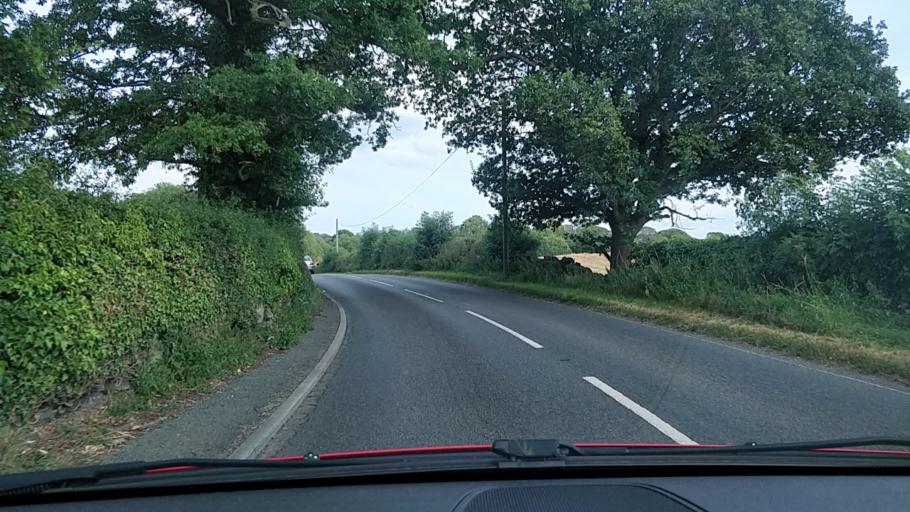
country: GB
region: Wales
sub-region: County of Flintshire
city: Penyffordd
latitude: 53.1414
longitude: -3.0626
